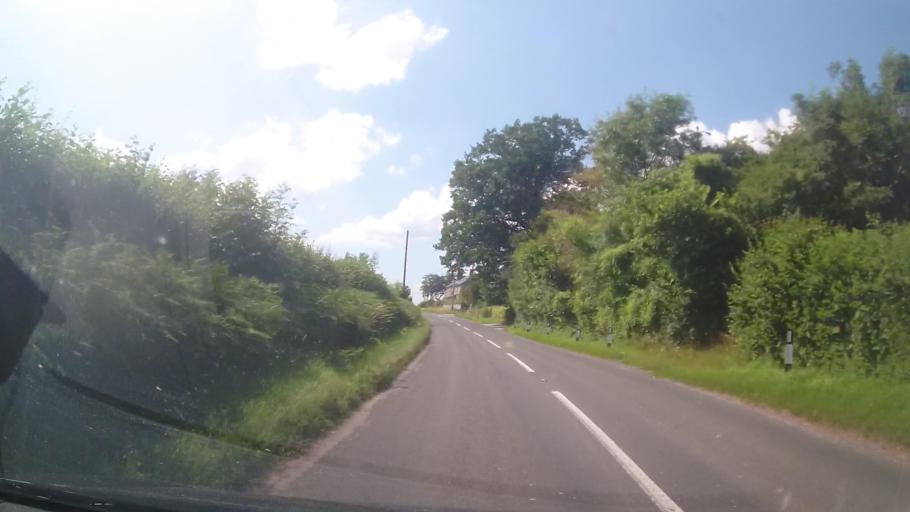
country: GB
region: England
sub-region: Herefordshire
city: Brockhampton
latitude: 52.0029
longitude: -2.5911
